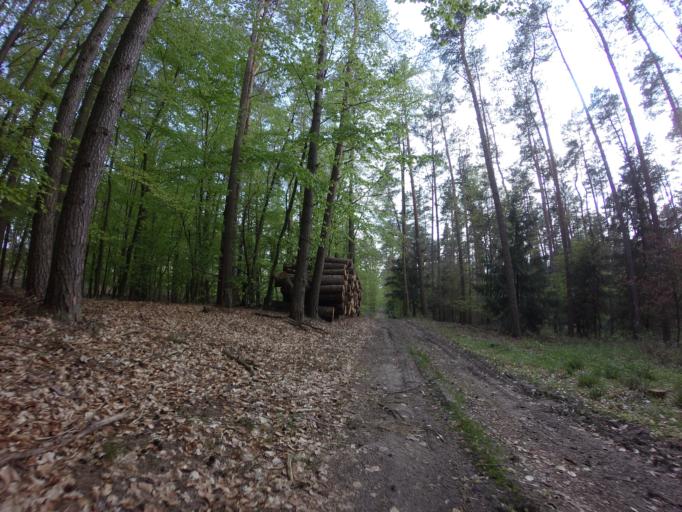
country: PL
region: West Pomeranian Voivodeship
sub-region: Powiat choszczenski
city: Choszczno
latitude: 53.1526
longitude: 15.3162
